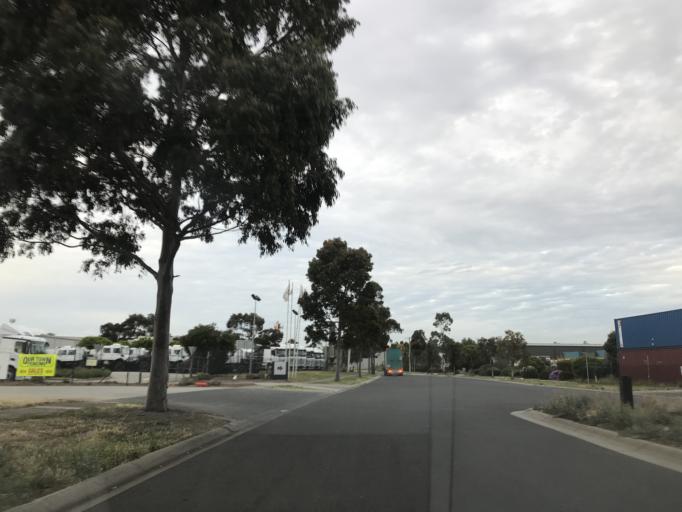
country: AU
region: Victoria
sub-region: Brimbank
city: Derrimut
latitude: -37.8121
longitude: 144.7824
